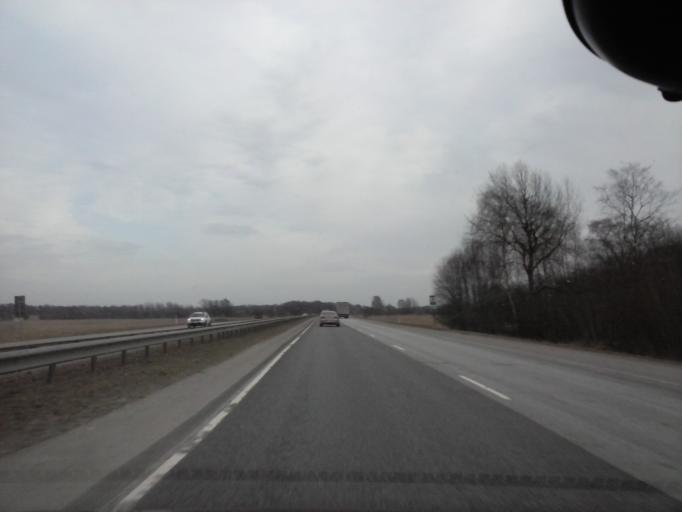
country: EE
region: Harju
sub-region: Rae vald
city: Jueri
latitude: 59.3425
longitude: 24.8989
